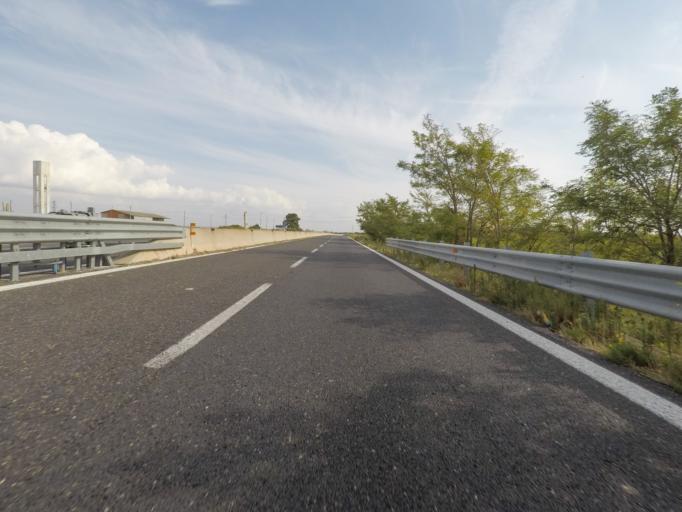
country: IT
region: Latium
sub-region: Provincia di Viterbo
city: Montalto di Castro
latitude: 42.3650
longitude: 11.5780
